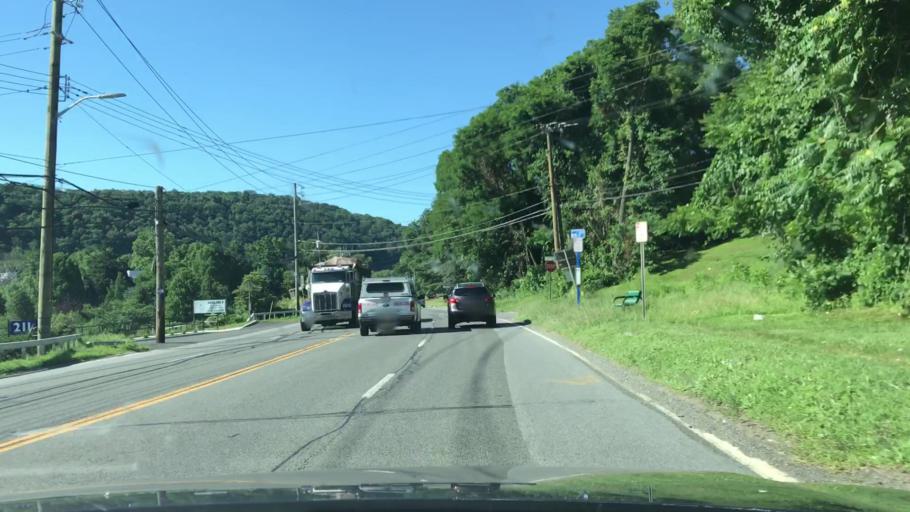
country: US
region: New York
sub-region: Westchester County
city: Hawthorne
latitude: 41.0997
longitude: -73.8078
